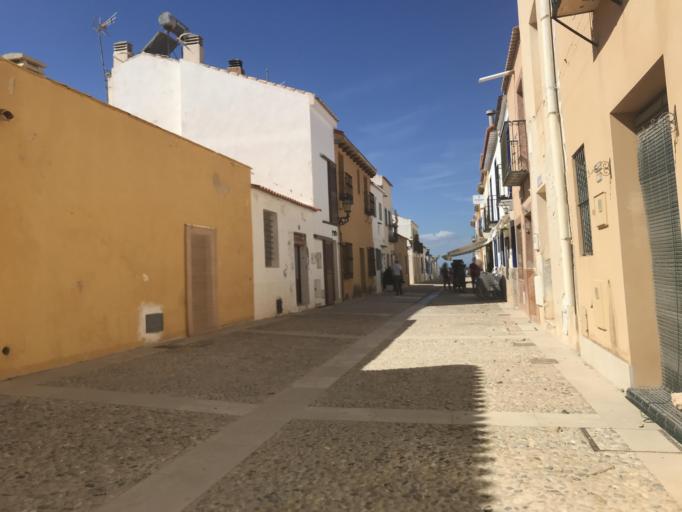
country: ES
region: Valencia
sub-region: Provincia de Alicante
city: Santa Pola
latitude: 38.1665
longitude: -0.4827
